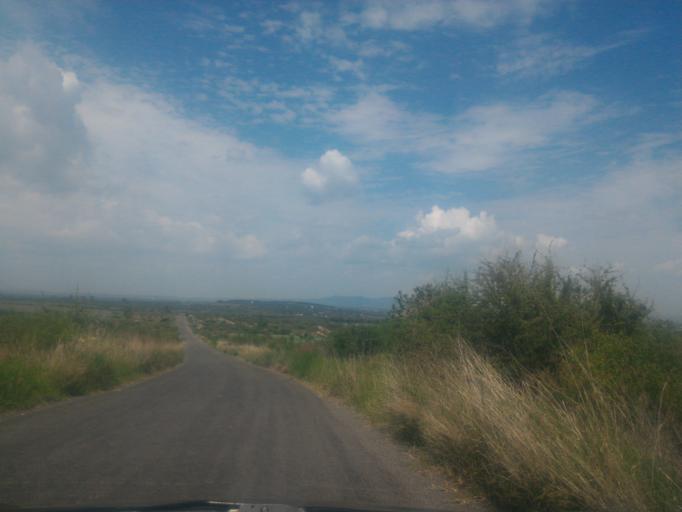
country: MX
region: Guanajuato
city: Ciudad Manuel Doblado
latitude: 20.8311
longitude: -102.0331
